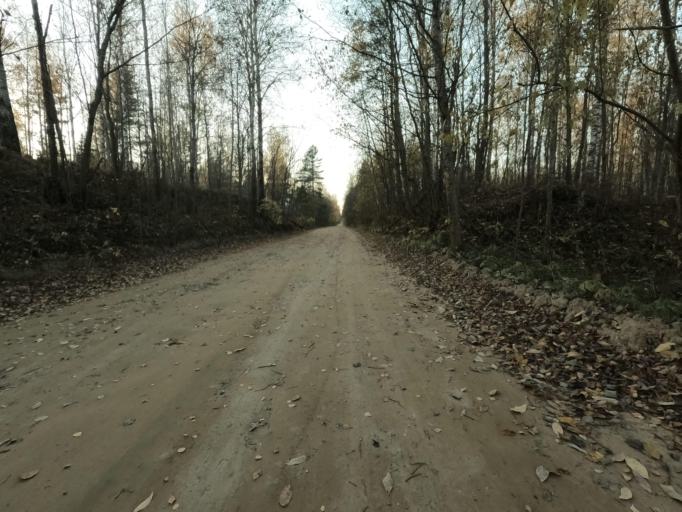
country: RU
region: Leningrad
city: Mga
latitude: 59.7575
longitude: 31.2717
